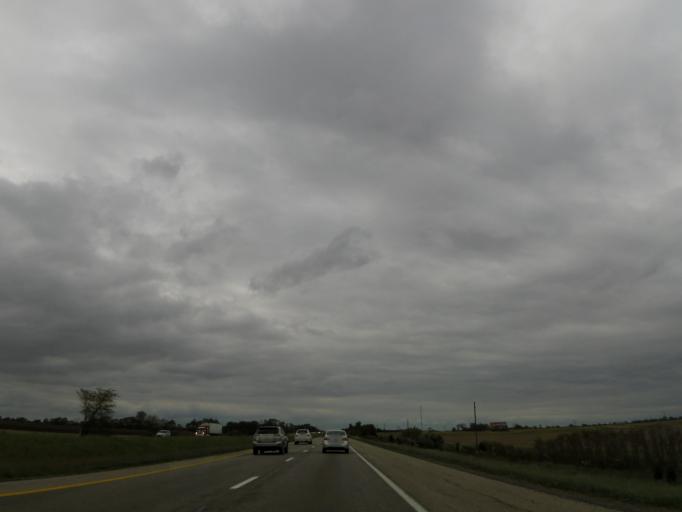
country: US
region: Ohio
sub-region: Madison County
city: Mount Sterling
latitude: 39.7985
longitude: -83.2186
